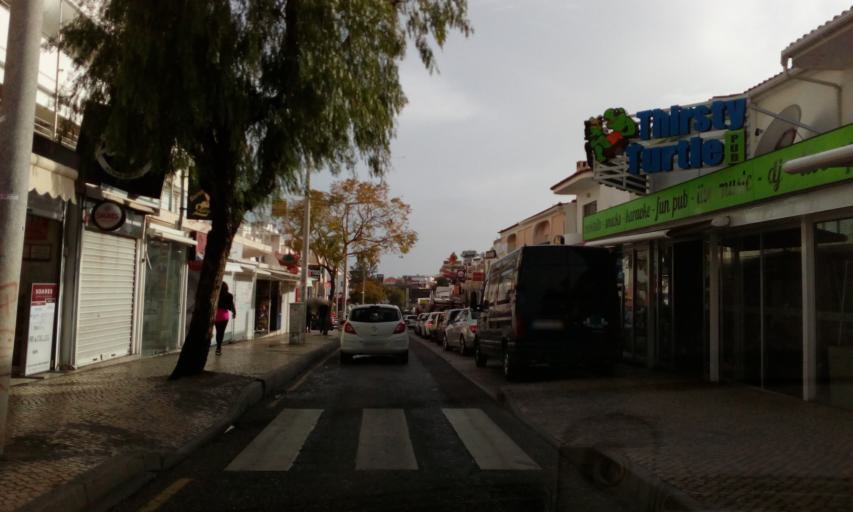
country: PT
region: Faro
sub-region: Albufeira
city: Albufeira
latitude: 37.0928
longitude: -8.2279
